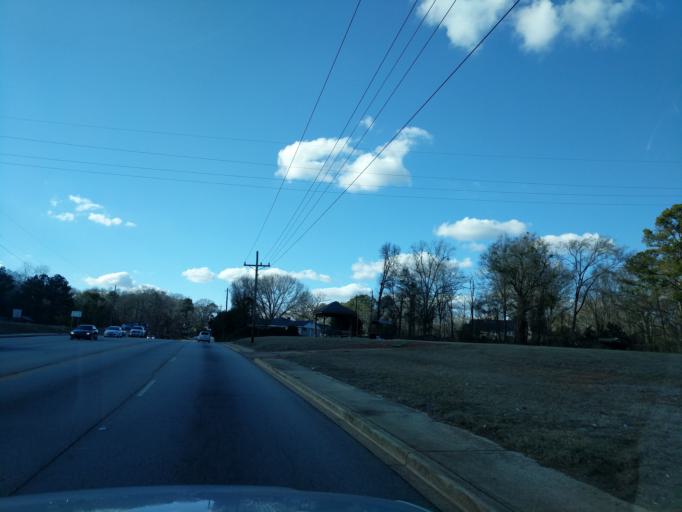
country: US
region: South Carolina
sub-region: Greenwood County
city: Greenwood
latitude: 34.2068
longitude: -82.1388
